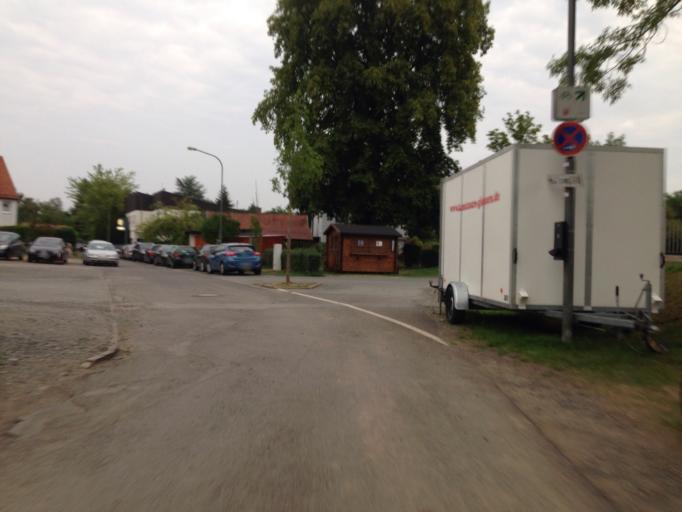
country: DE
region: Hesse
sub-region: Regierungsbezirk Giessen
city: Giessen
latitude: 50.5903
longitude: 8.6675
